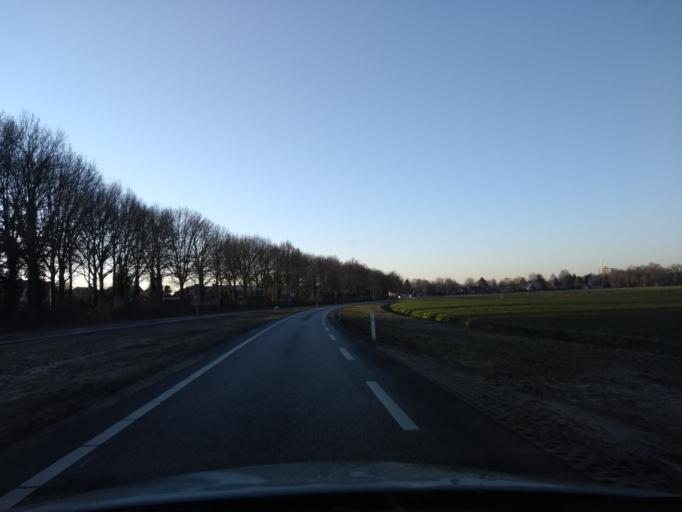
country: NL
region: Overijssel
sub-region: Gemeente Hof van Twente
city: Delden
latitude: 52.2643
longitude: 6.7024
